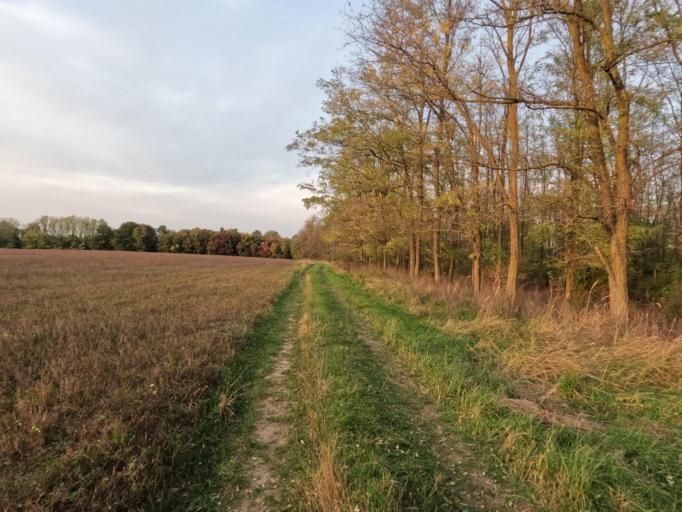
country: HU
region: Tolna
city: Szentgalpuszta
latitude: 46.3436
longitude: 18.6119
